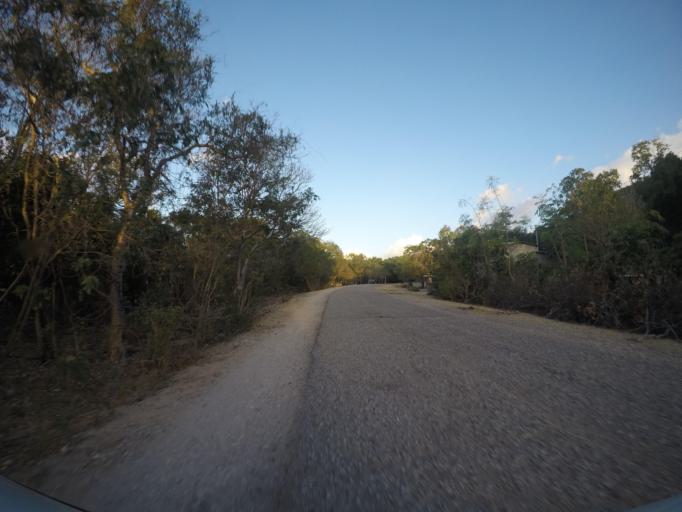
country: TL
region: Lautem
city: Lospalos
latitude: -8.3430
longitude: 127.0299
